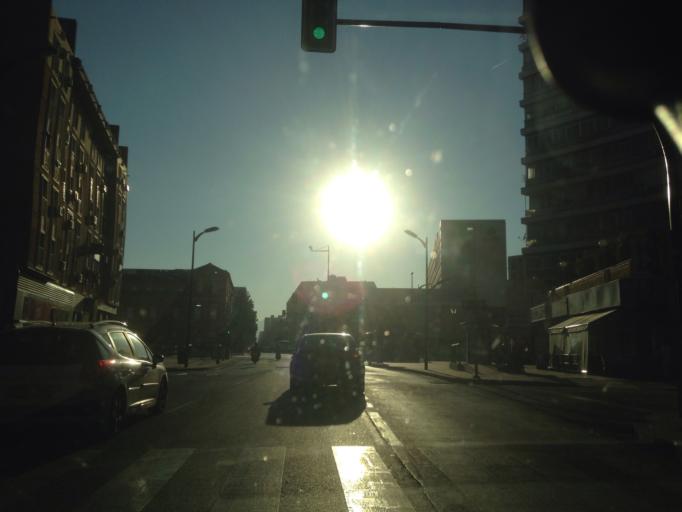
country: ES
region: Andalusia
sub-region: Provincia de Malaga
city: Malaga
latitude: 36.7124
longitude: -4.4296
